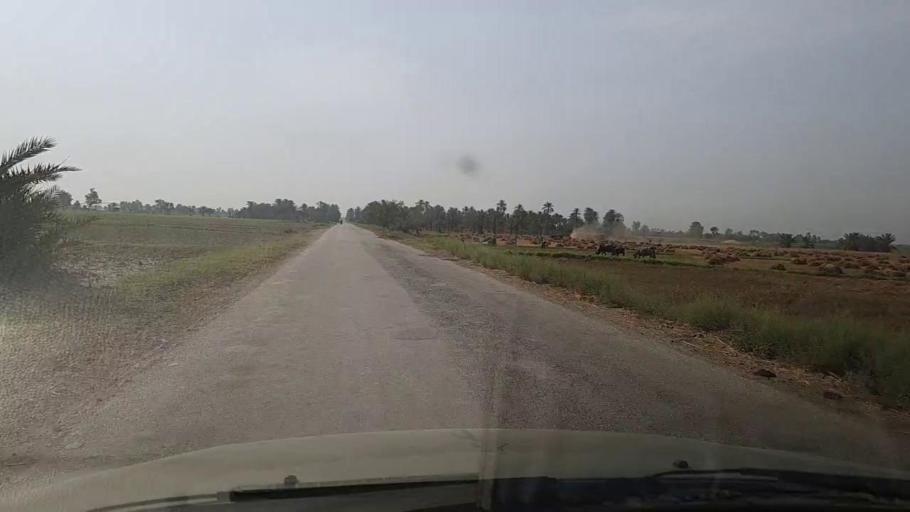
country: PK
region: Sindh
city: Gambat
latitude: 27.4714
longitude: 68.4748
